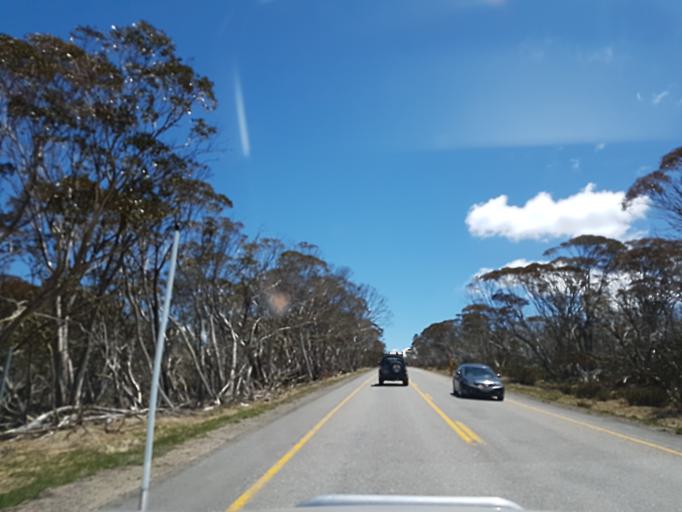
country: AU
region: Victoria
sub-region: Alpine
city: Mount Beauty
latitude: -37.0021
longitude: 147.1812
